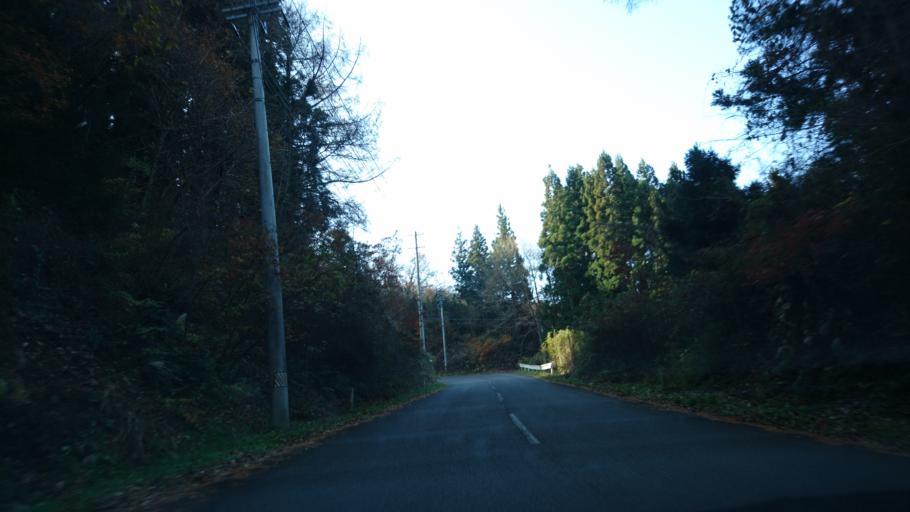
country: JP
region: Iwate
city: Ichinoseki
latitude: 38.8628
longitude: 141.3400
